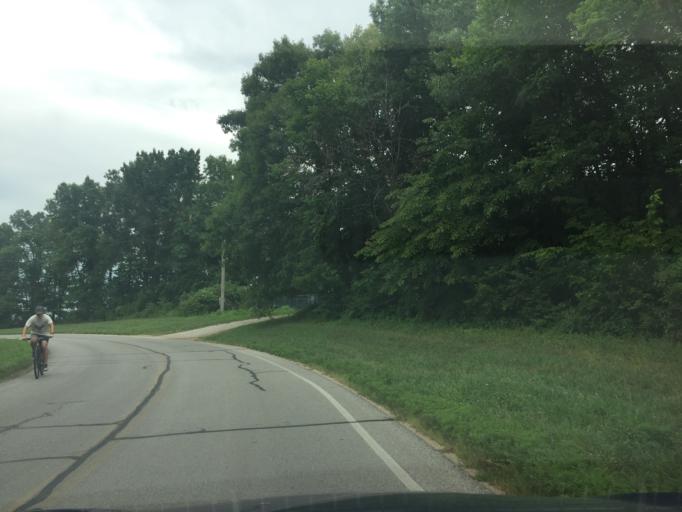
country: US
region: Kansas
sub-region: Leavenworth County
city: Leavenworth
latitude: 39.3515
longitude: -94.9412
